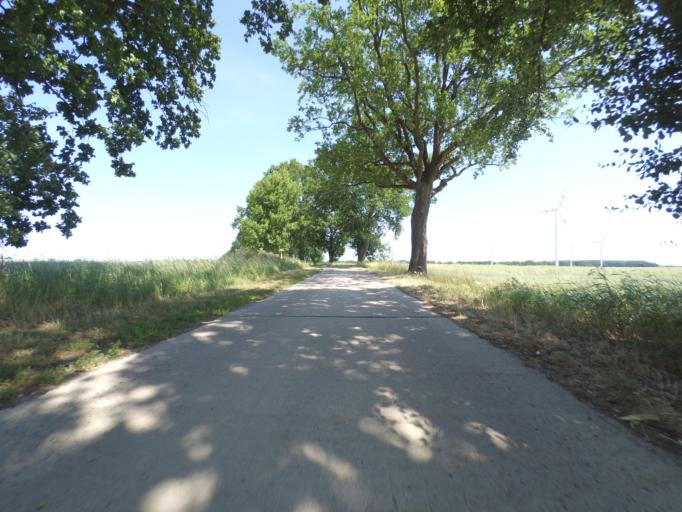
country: DE
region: Brandenburg
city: Gerdshagen
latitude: 53.2646
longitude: 12.2805
